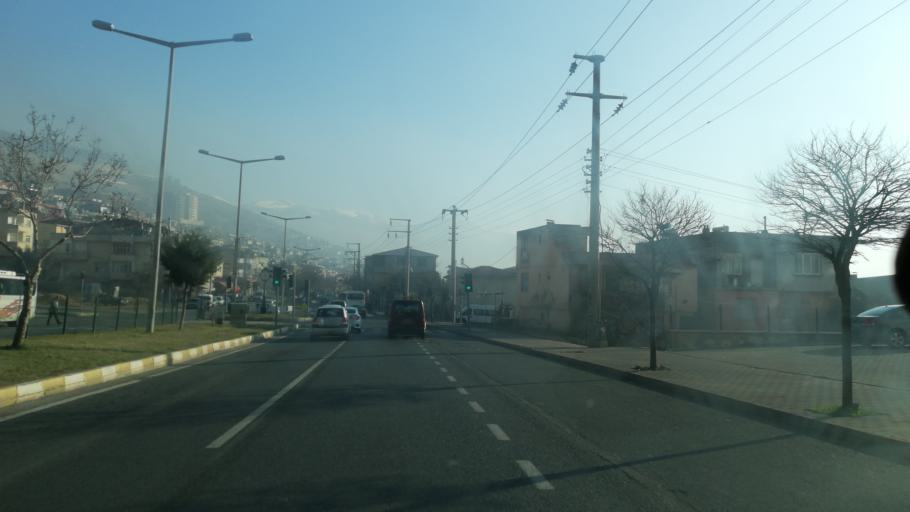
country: TR
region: Kahramanmaras
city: Kahramanmaras
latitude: 37.5933
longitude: 36.9044
